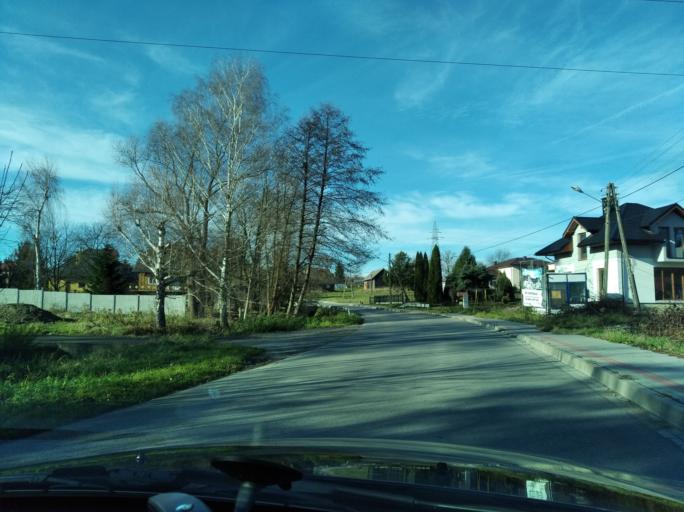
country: PL
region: Subcarpathian Voivodeship
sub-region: Powiat rzeszowski
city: Kielanowka
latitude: 50.0109
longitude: 21.9340
